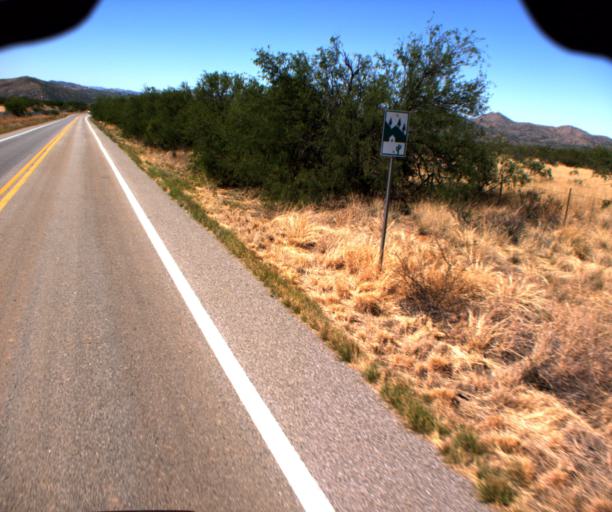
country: US
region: Arizona
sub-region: Santa Cruz County
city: Nogales
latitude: 31.4170
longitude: -110.8532
